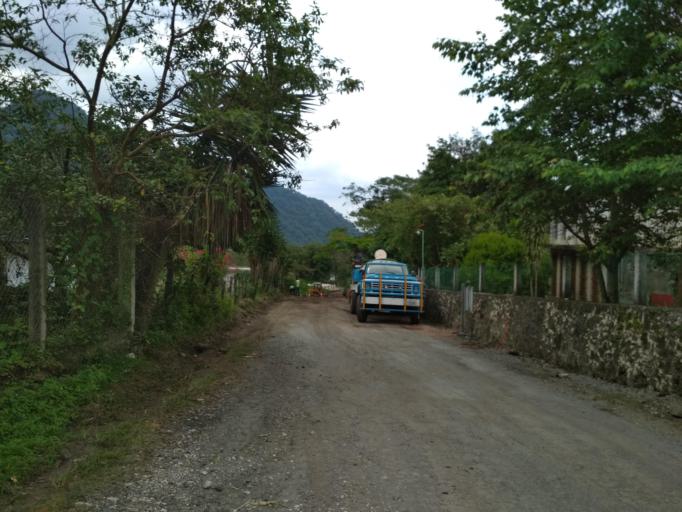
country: MX
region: Veracruz
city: Jilotepec
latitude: 19.6174
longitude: -96.9333
